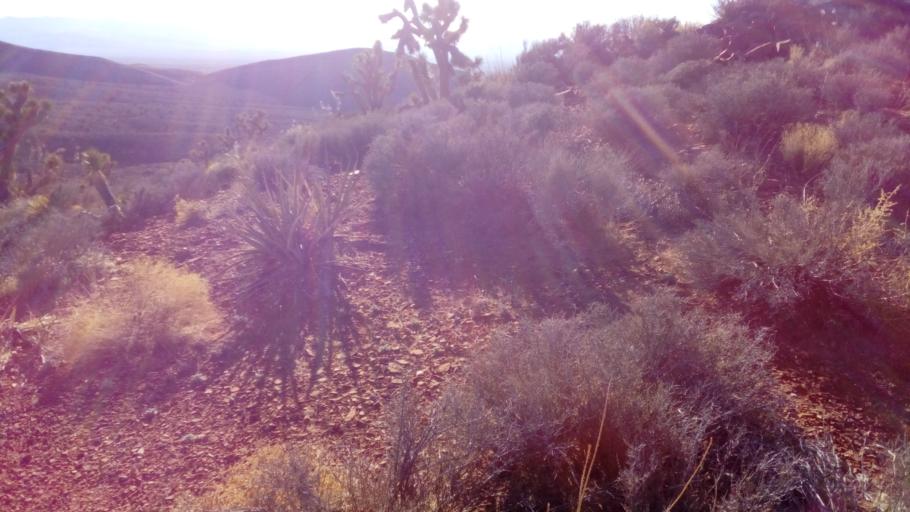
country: US
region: Nevada
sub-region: Clark County
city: Summerlin South
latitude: 36.0647
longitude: -115.5755
